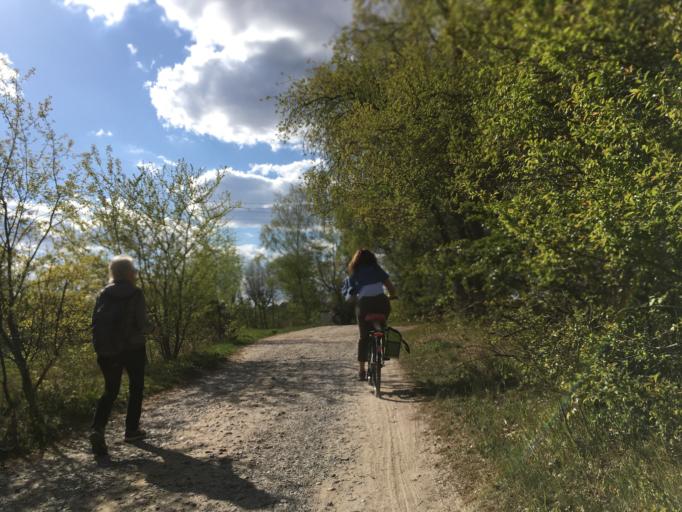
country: DE
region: Brandenburg
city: Wandlitz
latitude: 52.7526
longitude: 13.4291
